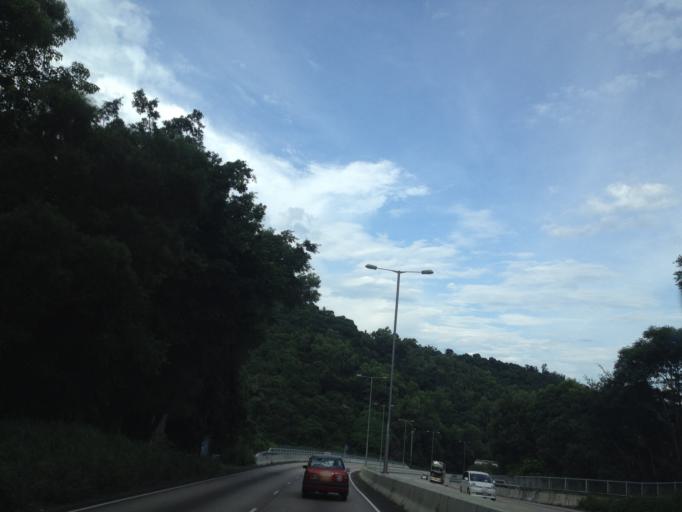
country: HK
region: Sha Tin
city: Sha Tin
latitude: 22.3820
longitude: 114.1707
